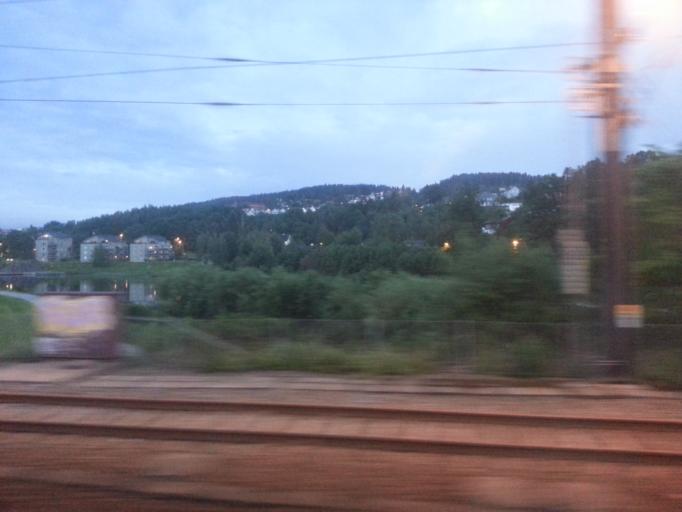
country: NO
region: Akershus
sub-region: Skedsmo
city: Lillestrom
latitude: 59.9524
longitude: 11.0388
